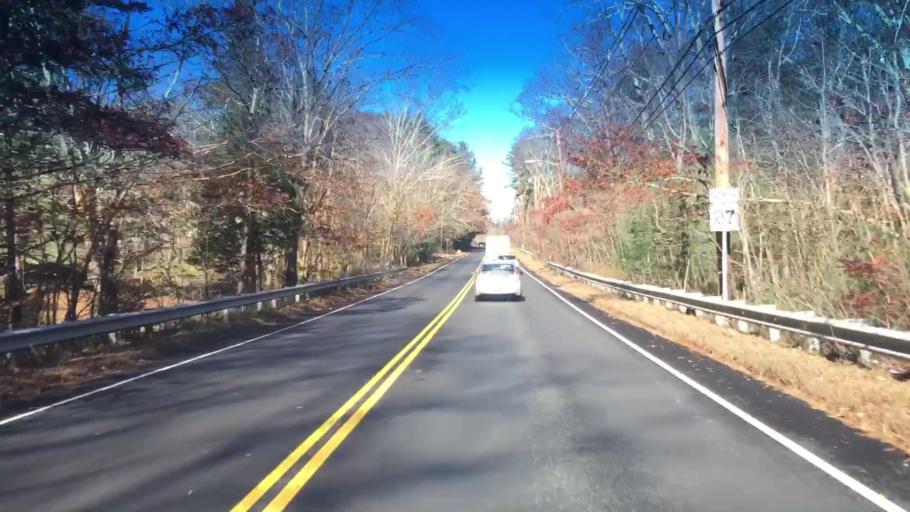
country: US
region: Massachusetts
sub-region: Norfolk County
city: Walpole
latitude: 42.1551
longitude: -71.2720
